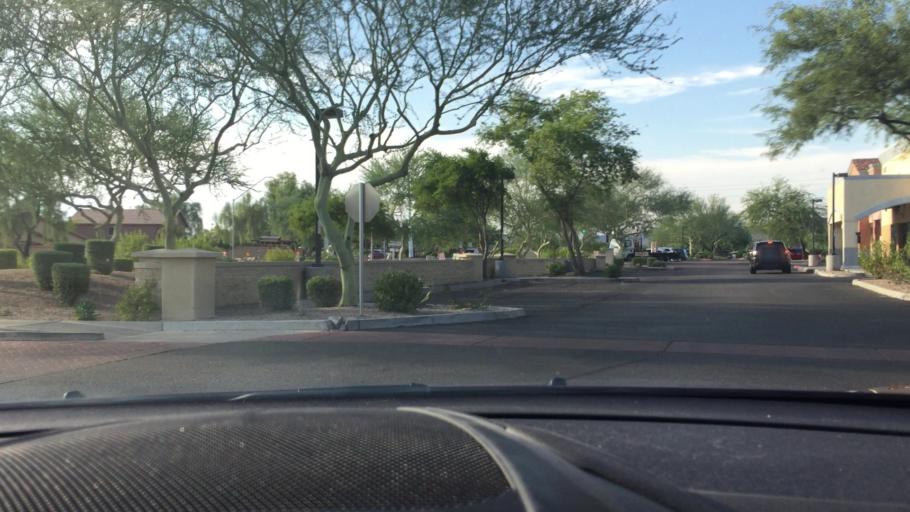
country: US
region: Arizona
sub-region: Maricopa County
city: Peoria
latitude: 33.6528
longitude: -112.1859
